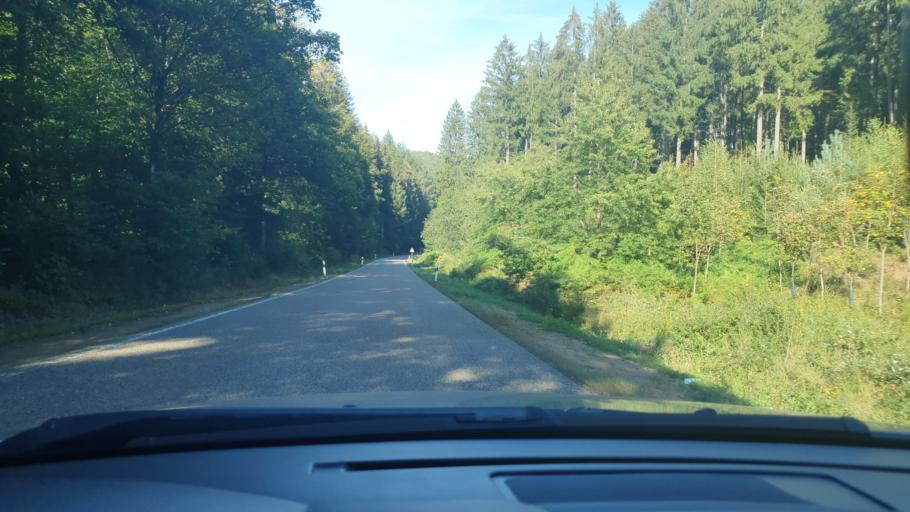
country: DE
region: Rheinland-Pfalz
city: Heltersberg
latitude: 49.3214
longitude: 7.7162
